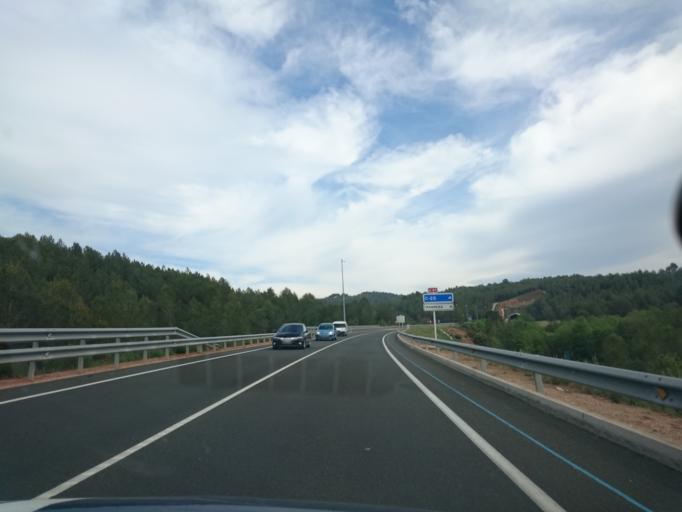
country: ES
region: Catalonia
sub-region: Provincia de Barcelona
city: Sant Salvador de Guardiola
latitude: 41.7008
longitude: 1.7788
